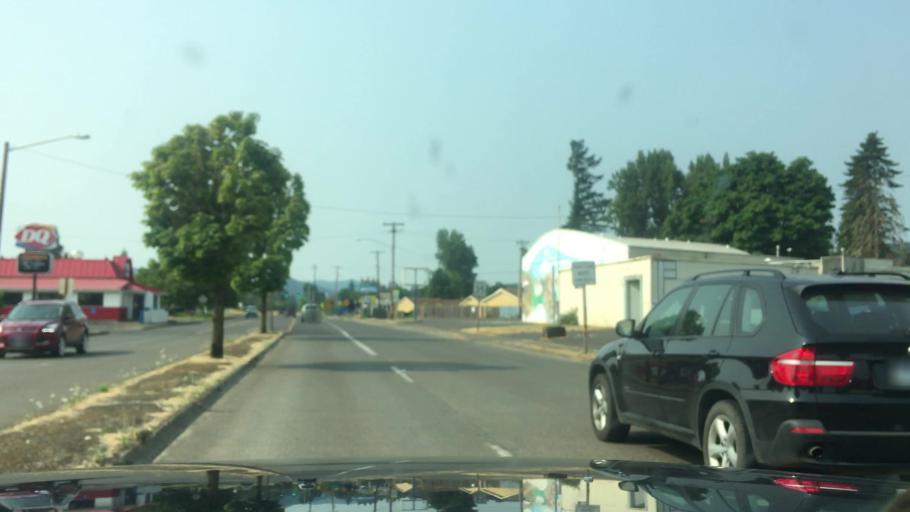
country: US
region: Oregon
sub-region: Lane County
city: Cottage Grove
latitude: 43.7922
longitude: -123.0630
